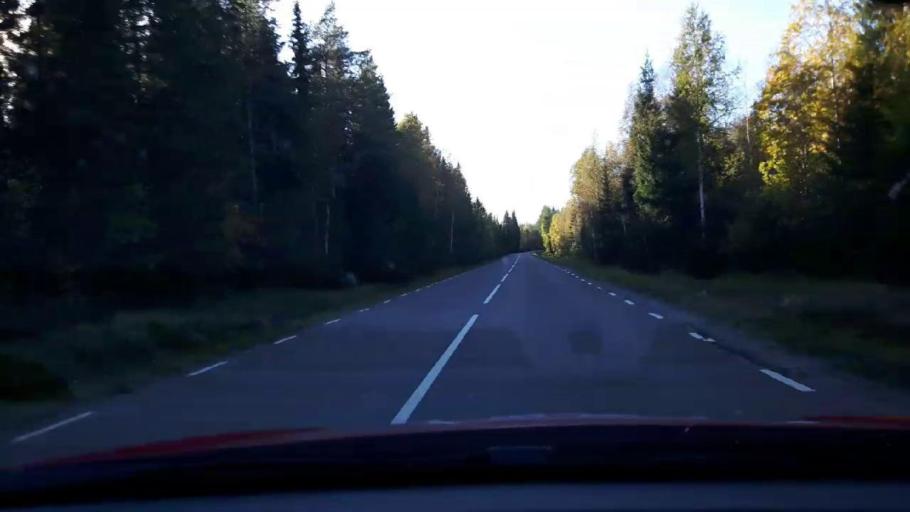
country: SE
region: Jaemtland
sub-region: Stroemsunds Kommun
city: Stroemsund
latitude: 63.8424
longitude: 15.4351
